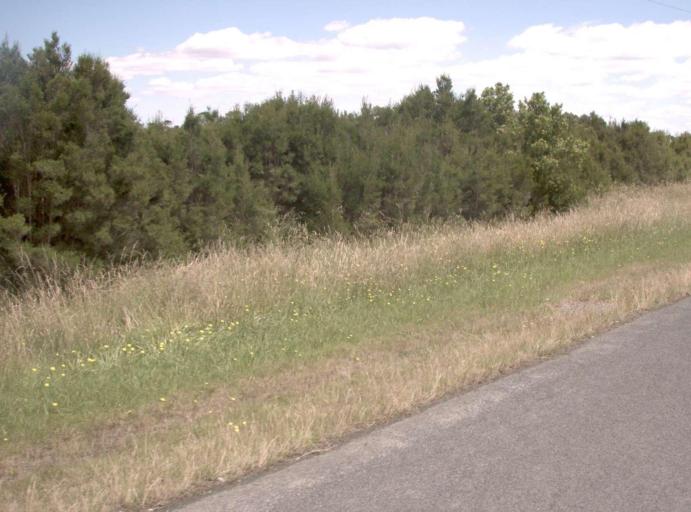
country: AU
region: Victoria
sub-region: Cardinia
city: Koo-Wee-Rup
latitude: -38.2967
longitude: 145.5440
